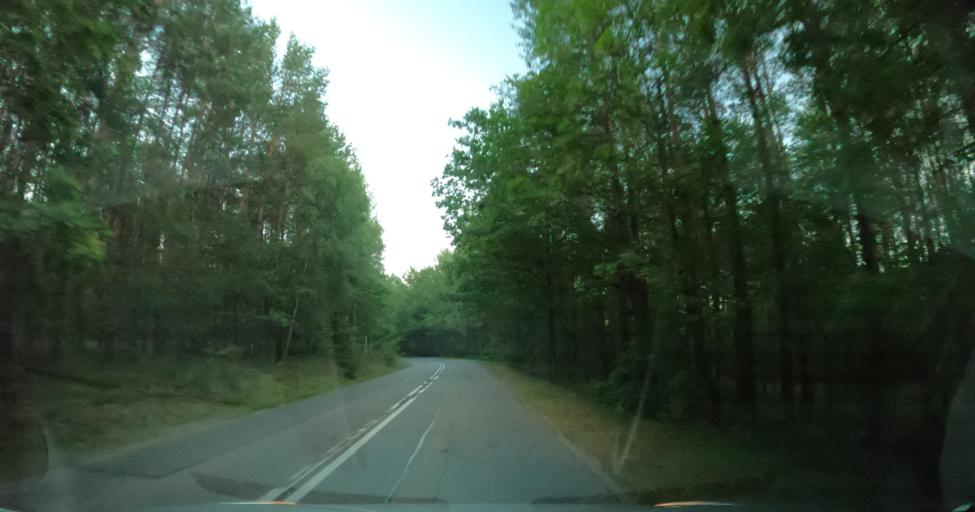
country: PL
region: Pomeranian Voivodeship
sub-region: Powiat wejherowski
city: Linia
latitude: 54.4632
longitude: 17.9961
